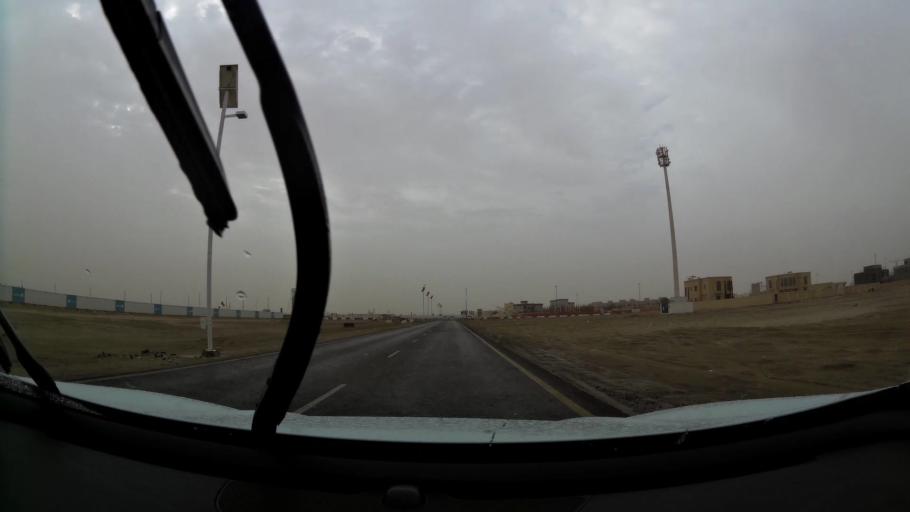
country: AE
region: Abu Dhabi
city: Abu Dhabi
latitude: 24.4265
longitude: 54.6062
